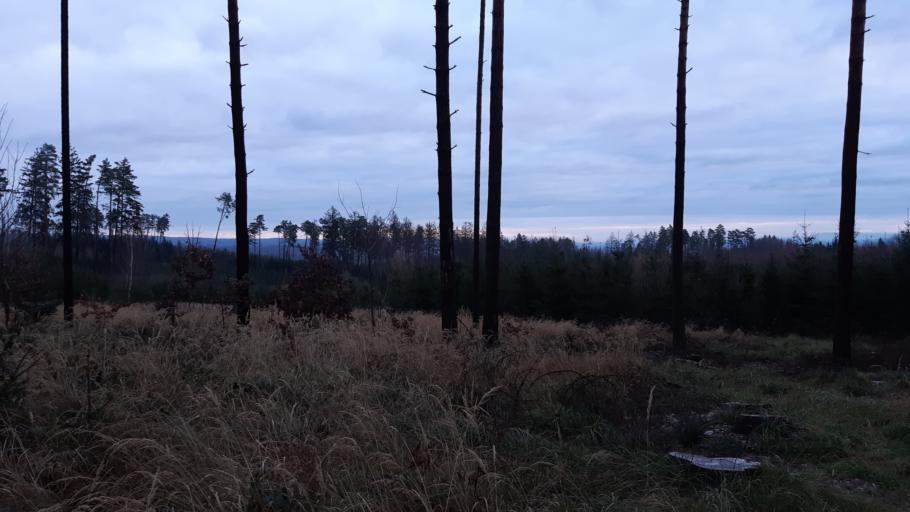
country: CZ
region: South Moravian
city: Drnovice
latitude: 49.2666
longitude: 16.9201
